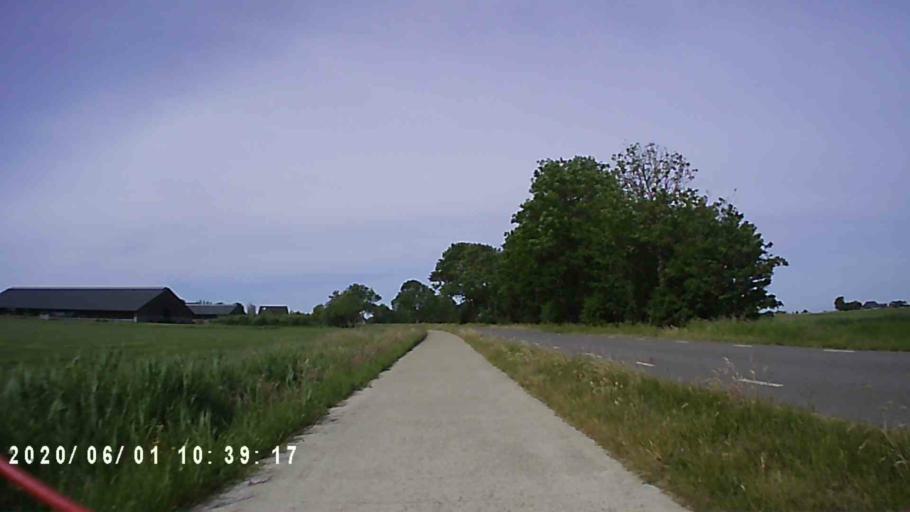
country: NL
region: Friesland
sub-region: Gemeente Franekeradeel
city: Tzummarum
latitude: 53.2167
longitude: 5.5717
